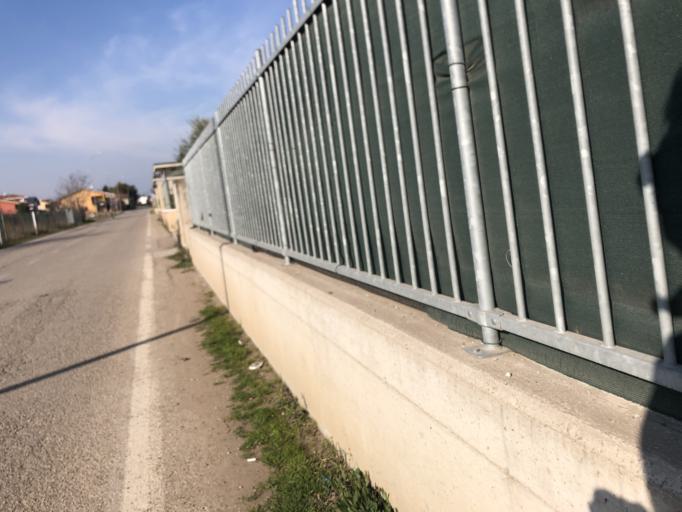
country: IT
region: Veneto
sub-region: Provincia di Verona
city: Lugagnano
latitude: 45.4291
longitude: 10.8815
